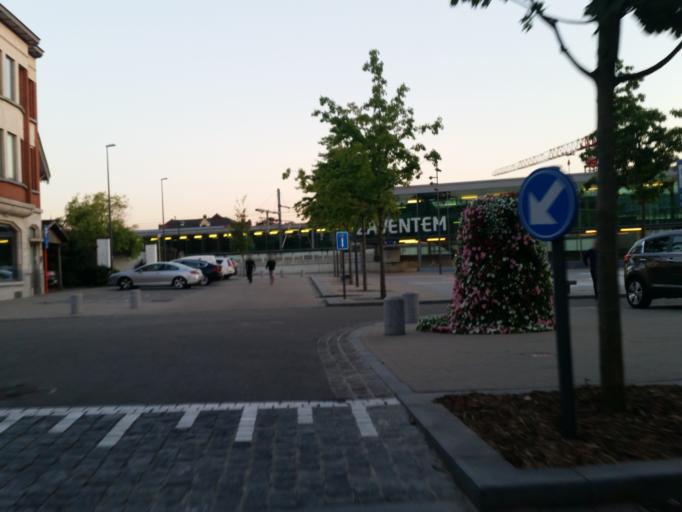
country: BE
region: Flanders
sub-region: Provincie Vlaams-Brabant
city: Zaventem
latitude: 50.8862
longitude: 4.4709
